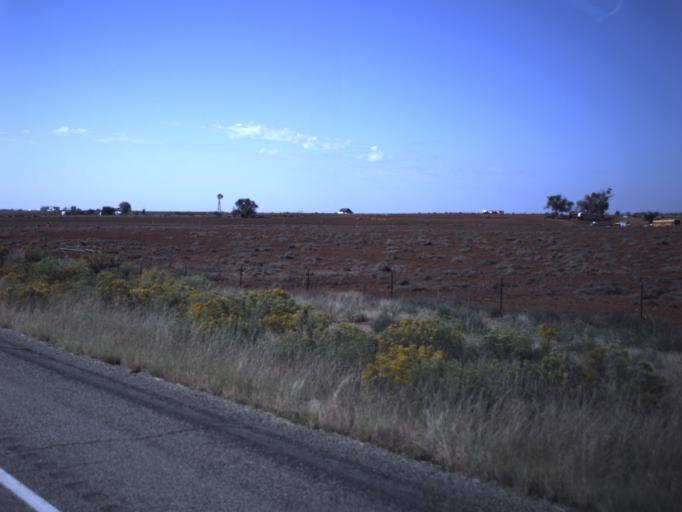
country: US
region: Utah
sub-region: San Juan County
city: Blanding
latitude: 37.5662
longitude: -109.4895
